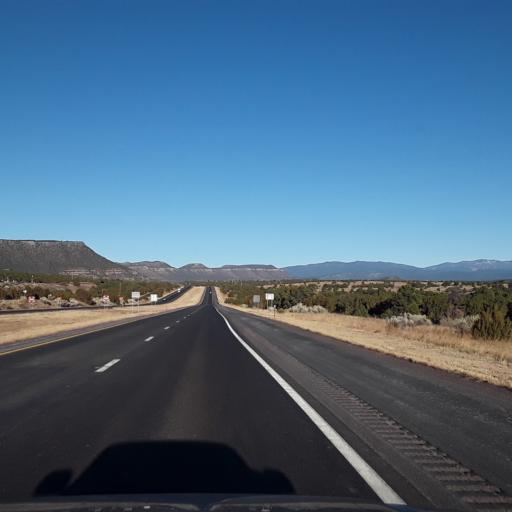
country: US
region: New Mexico
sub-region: San Miguel County
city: Pecos
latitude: 35.4381
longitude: -105.6087
